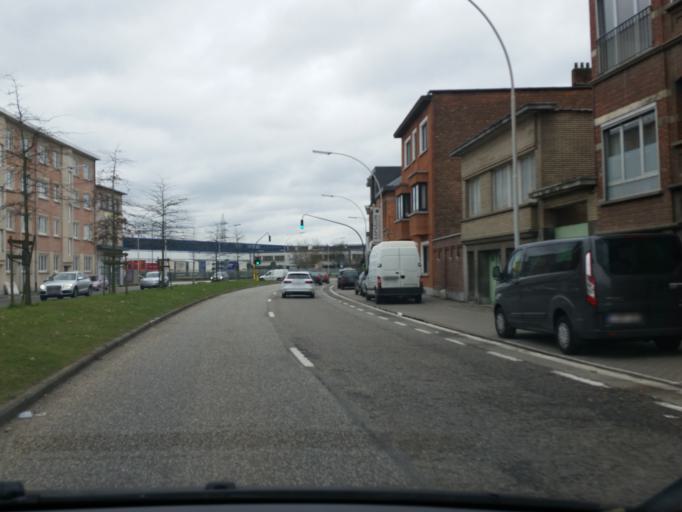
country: BE
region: Flanders
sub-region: Provincie Vlaams-Brabant
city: Vilvoorde
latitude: 50.9221
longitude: 4.4271
